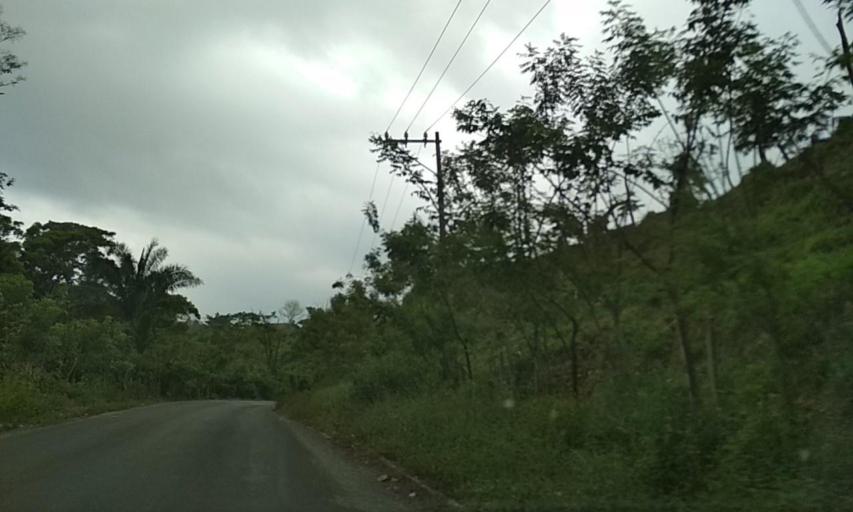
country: MX
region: Tabasco
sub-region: Huimanguillo
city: Francisco Rueda
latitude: 17.6435
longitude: -94.0936
